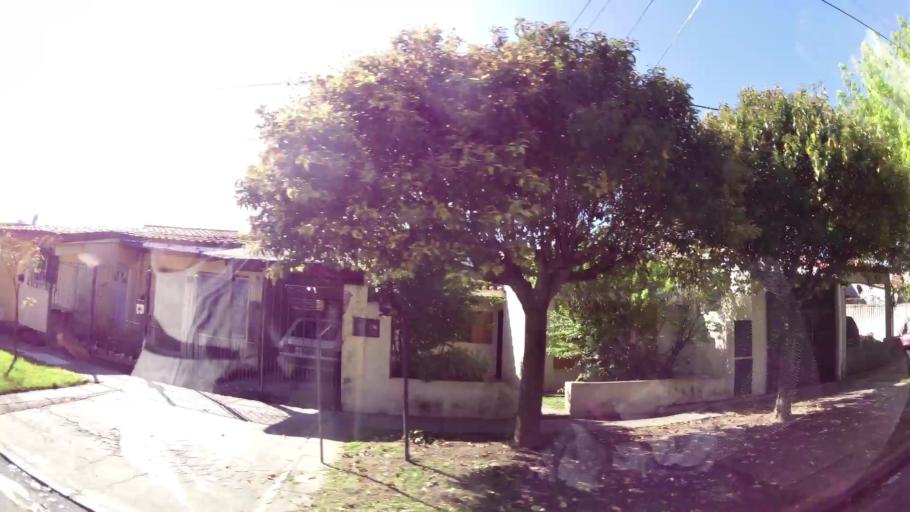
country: AR
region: Buenos Aires
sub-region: Partido de Quilmes
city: Quilmes
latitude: -34.7883
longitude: -58.1488
